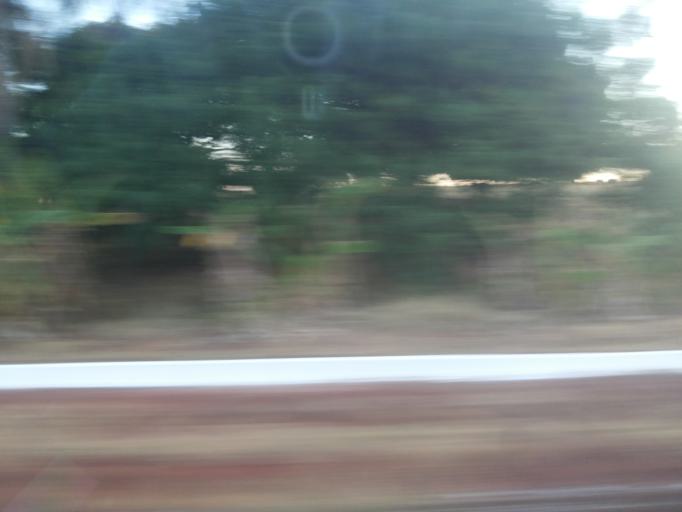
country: BR
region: Minas Gerais
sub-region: Capinopolis
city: Capinopolis
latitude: -18.7480
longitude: -49.5442
